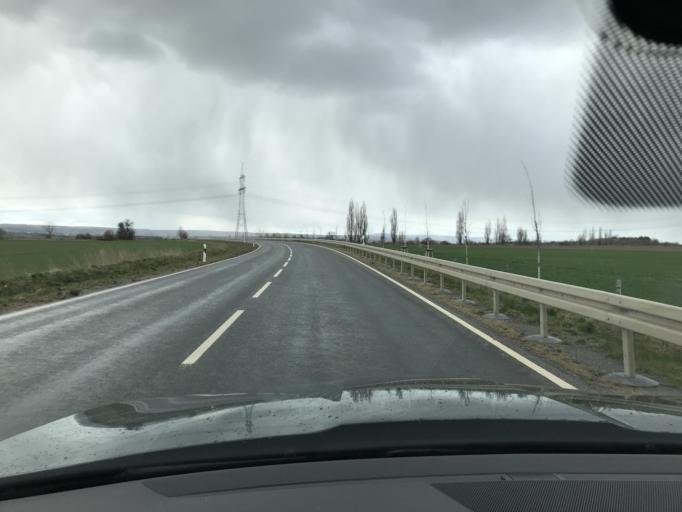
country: DE
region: Saxony-Anhalt
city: Hoym
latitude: 51.7685
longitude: 11.2912
